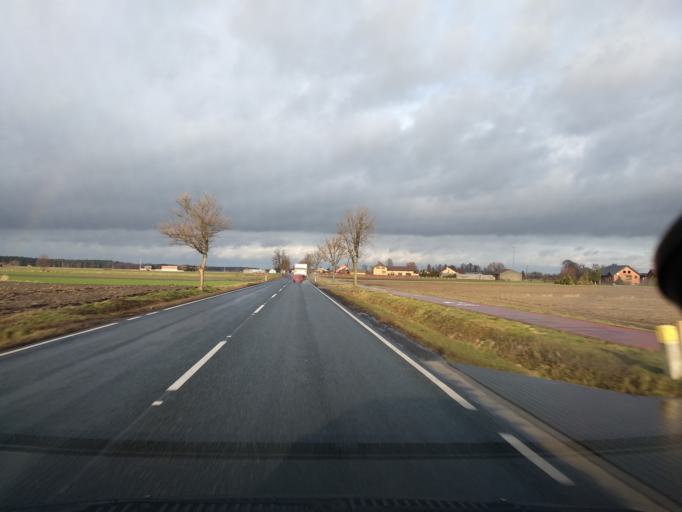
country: PL
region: Greater Poland Voivodeship
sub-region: Powiat koninski
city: Rychwal
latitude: 52.1092
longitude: 18.1675
